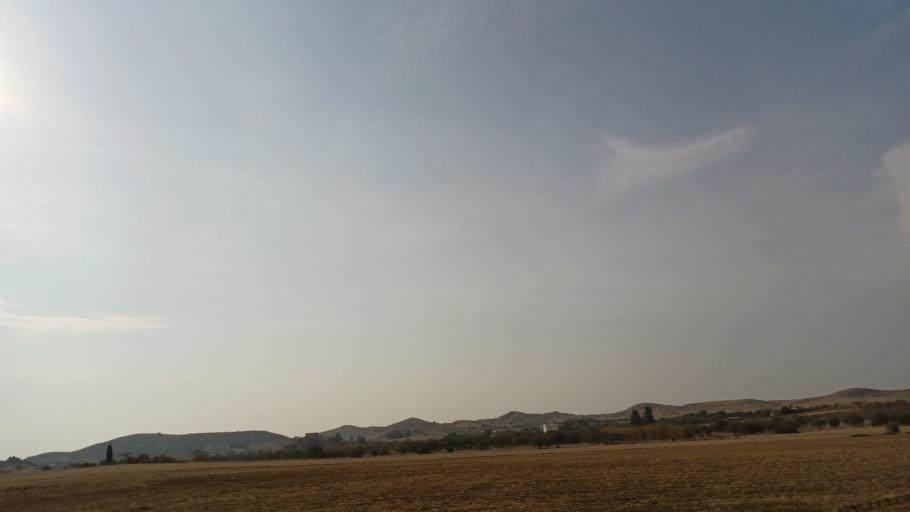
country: CY
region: Larnaka
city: Troulloi
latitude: 35.0328
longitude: 33.6055
